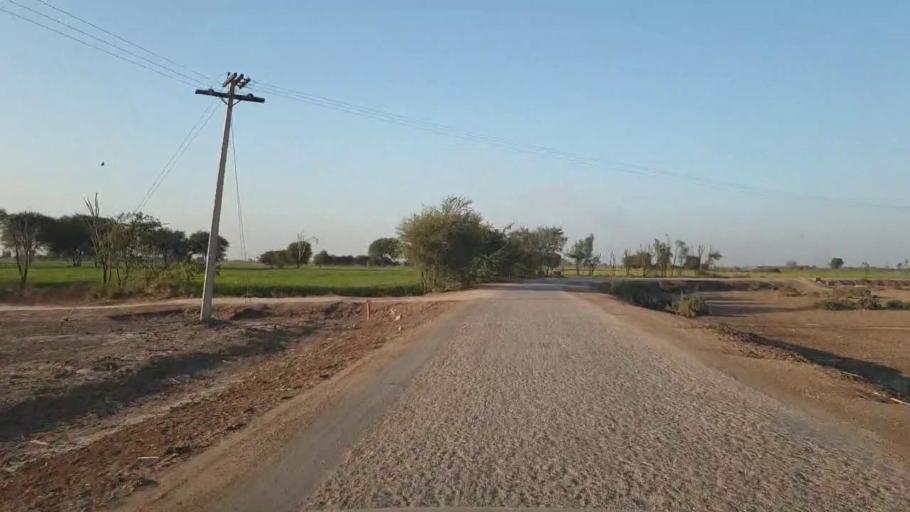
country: PK
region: Sindh
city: Tando Allahyar
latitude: 25.3763
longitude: 68.7479
